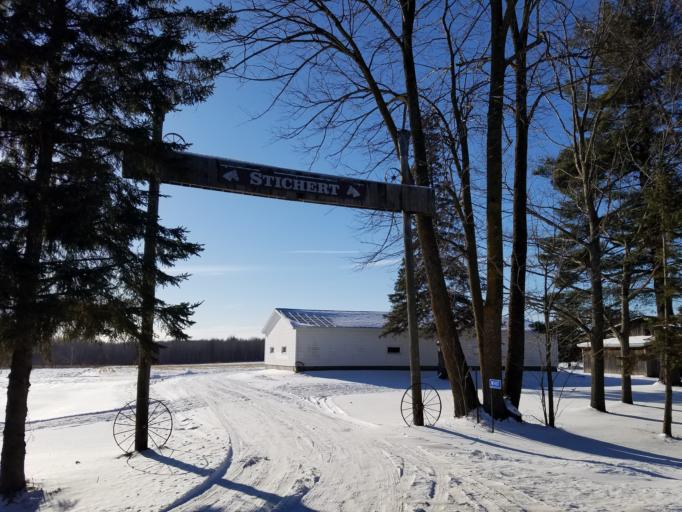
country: US
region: Wisconsin
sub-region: Clark County
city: Loyal
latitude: 44.6119
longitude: -90.3861
